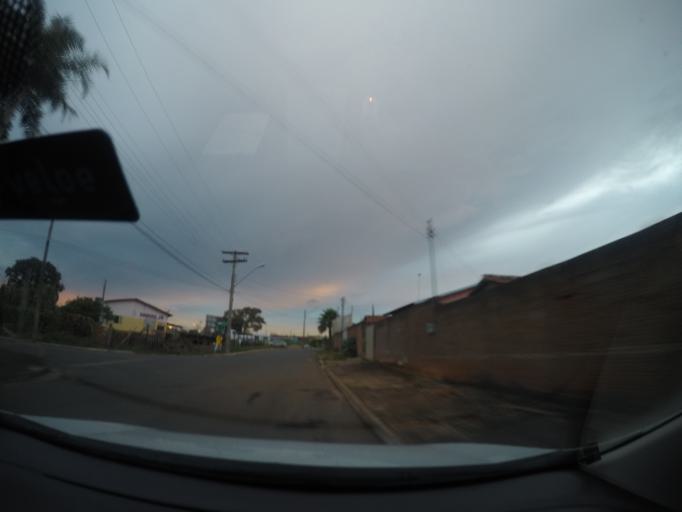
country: BR
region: Goias
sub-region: Goiania
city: Goiania
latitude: -16.7197
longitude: -49.3722
